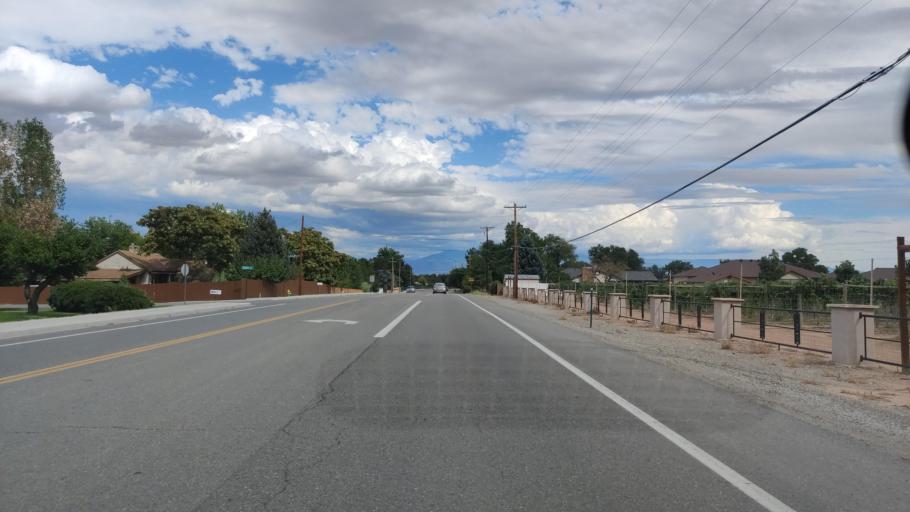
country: US
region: Colorado
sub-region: Mesa County
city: Redlands
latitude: 39.0924
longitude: -108.6620
